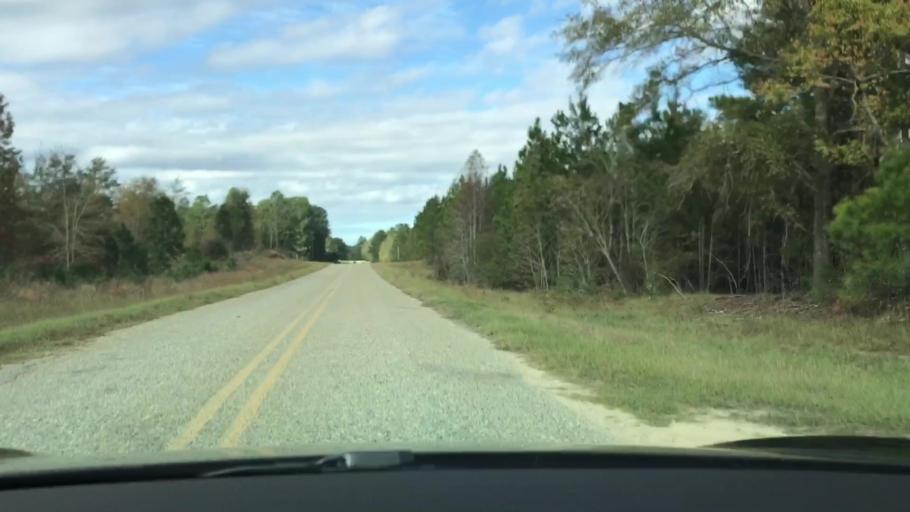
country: US
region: Georgia
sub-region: Jefferson County
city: Wadley
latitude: 32.8095
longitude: -82.3380
